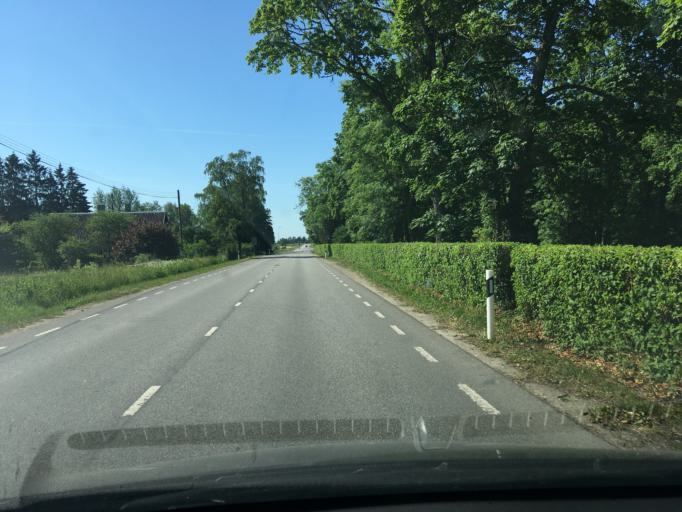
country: EE
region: Harju
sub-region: Raasiku vald
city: Raasiku
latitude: 59.3779
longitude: 25.1944
